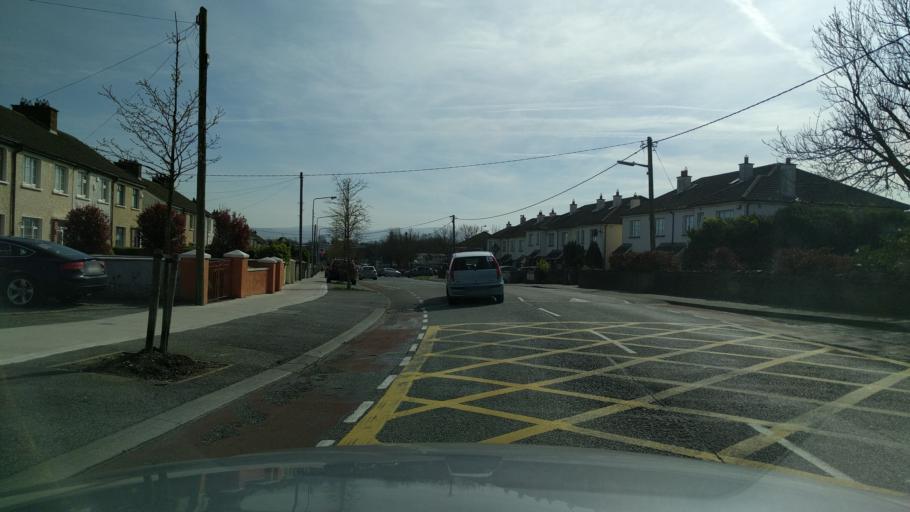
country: IE
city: Palmerstown
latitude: 53.3520
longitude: -6.3781
